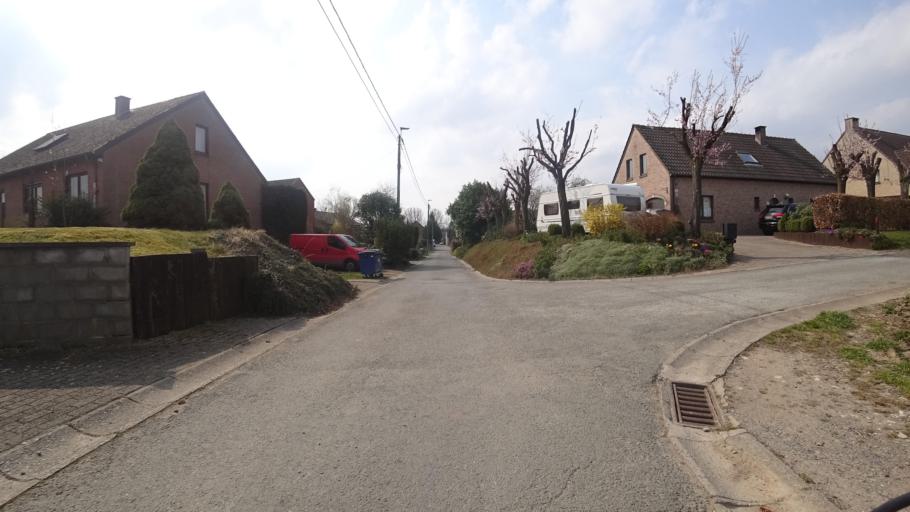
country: BE
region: Wallonia
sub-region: Province du Brabant Wallon
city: Chastre-Villeroux-Blanmont
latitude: 50.6114
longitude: 4.6546
